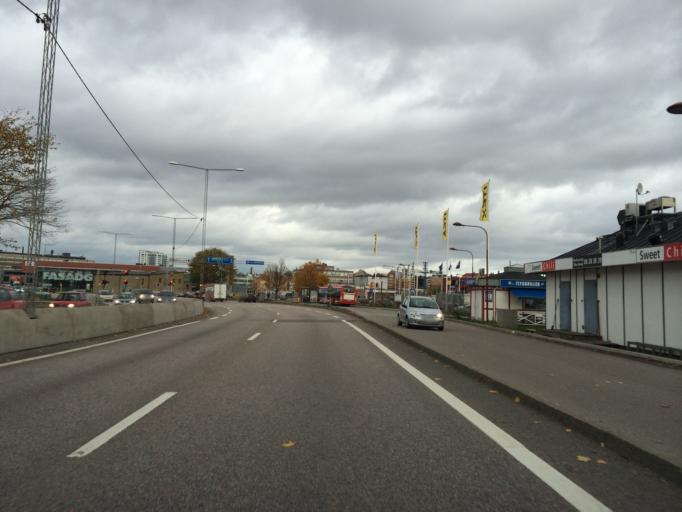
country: SE
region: Stockholm
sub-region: Sundbybergs Kommun
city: Sundbyberg
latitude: 59.3529
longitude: 17.9583
